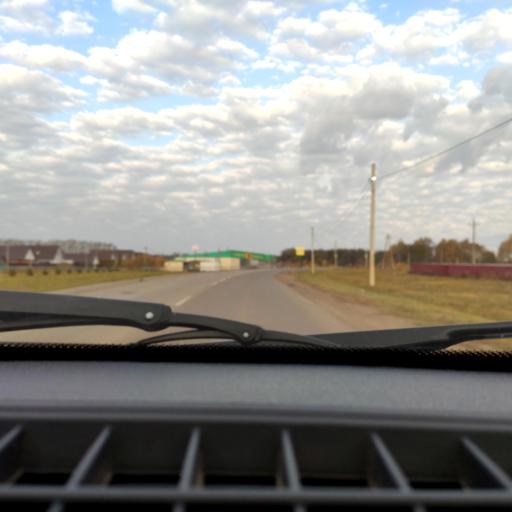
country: RU
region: Bashkortostan
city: Avdon
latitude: 54.6597
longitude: 55.7395
